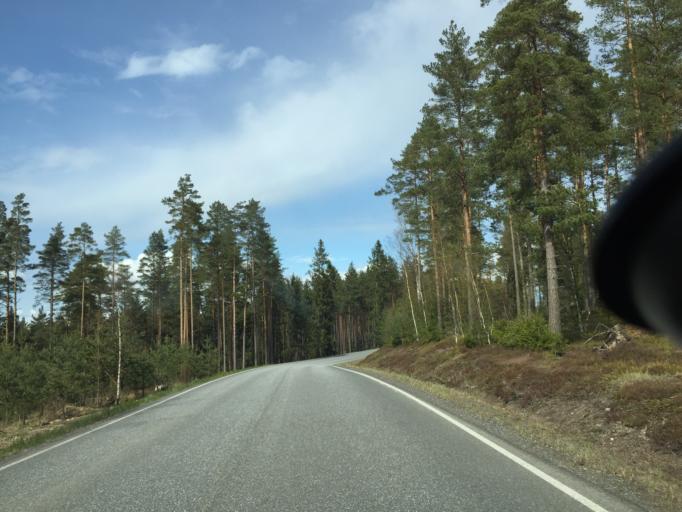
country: FI
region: Varsinais-Suomi
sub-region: Salo
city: Pernioe
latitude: 60.0302
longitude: 23.1829
